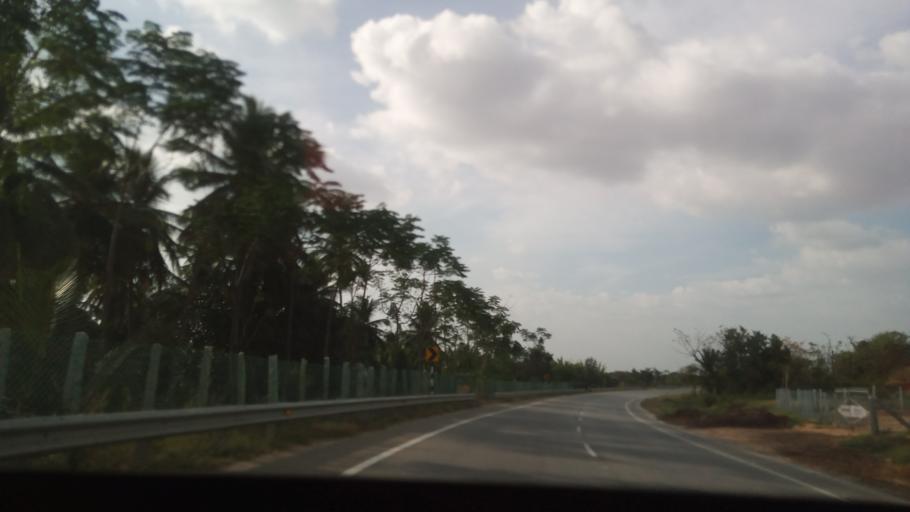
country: IN
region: Karnataka
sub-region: Tumkur
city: Kunigal
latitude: 12.8191
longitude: 77.0287
